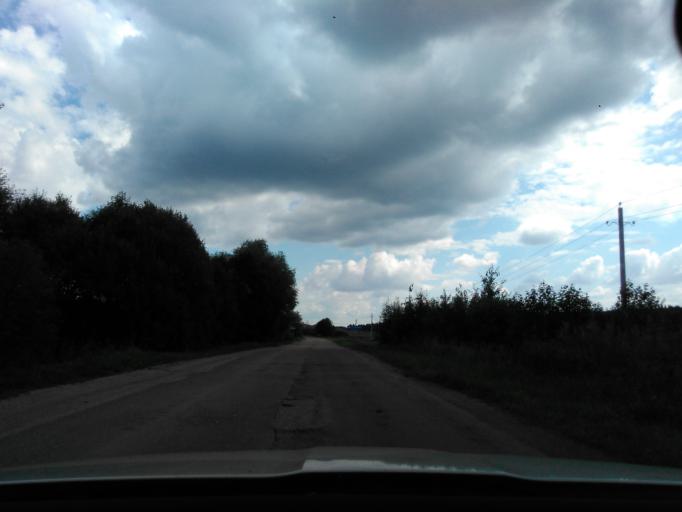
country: RU
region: Moskovskaya
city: Mendeleyevo
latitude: 56.1088
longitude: 37.2413
